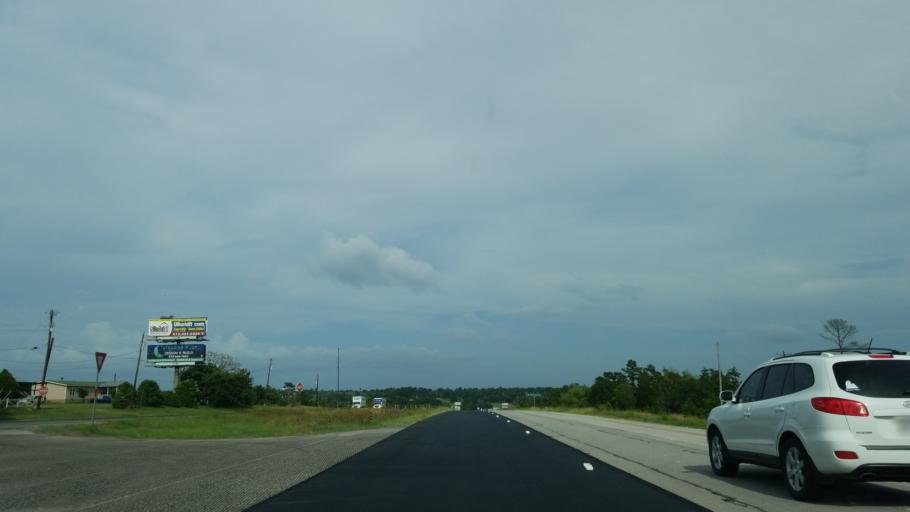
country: US
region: Texas
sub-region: Bastrop County
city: Smithville
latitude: 30.0708
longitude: -97.2285
